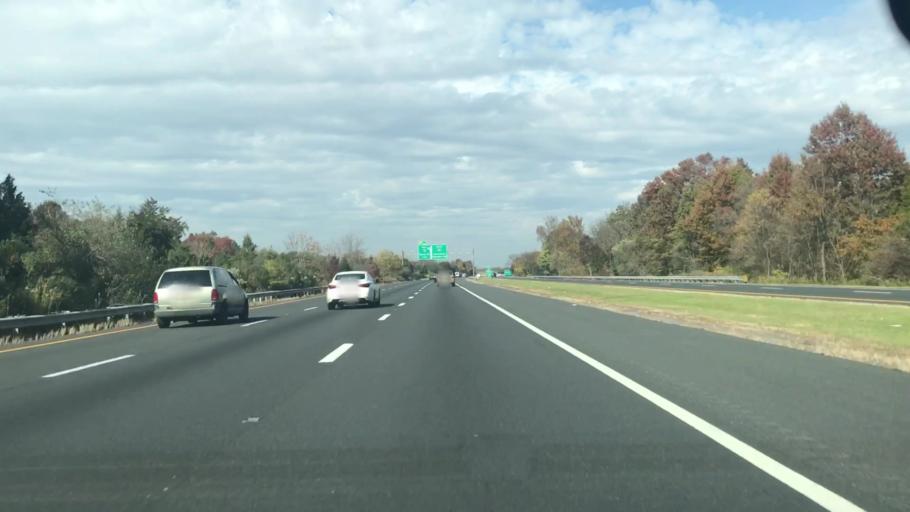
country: US
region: New Jersey
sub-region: Somerset County
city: Bridgewater
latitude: 40.6198
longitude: -74.6368
